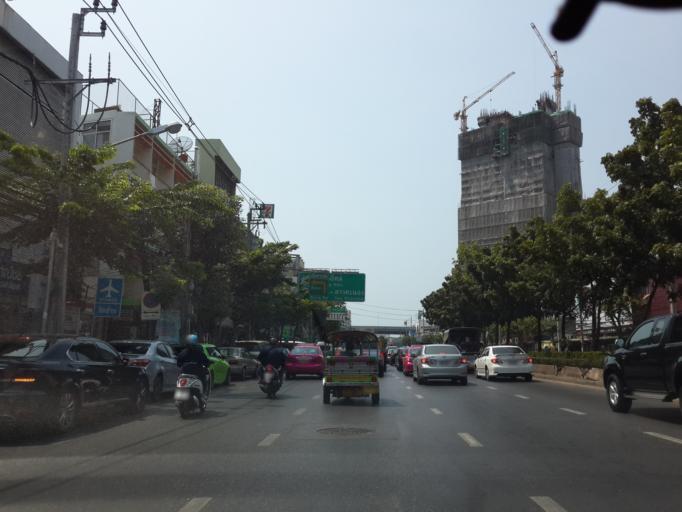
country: TH
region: Bangkok
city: Pathum Wan
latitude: 13.7350
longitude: 100.5231
